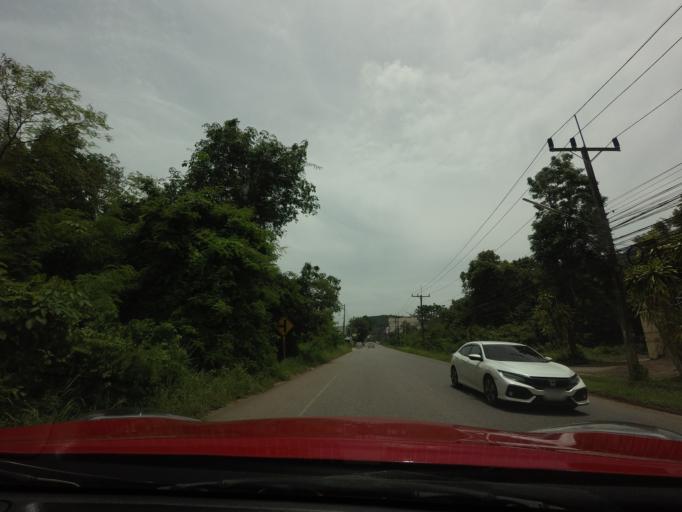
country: TH
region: Songkhla
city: Hat Yai
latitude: 7.0003
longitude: 100.5216
